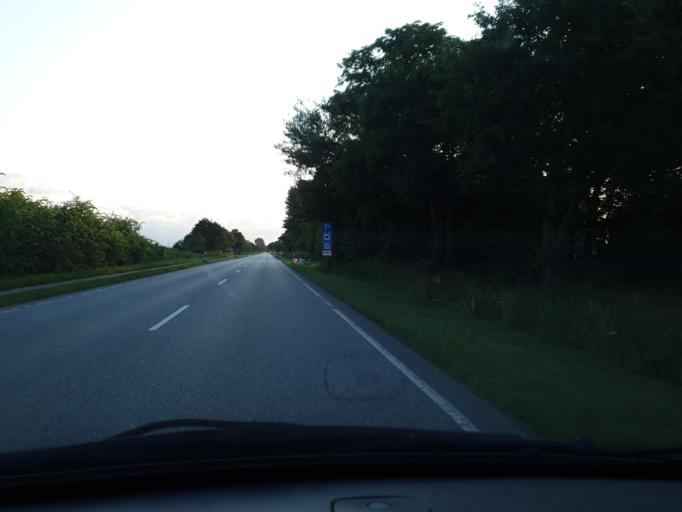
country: DE
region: Schleswig-Holstein
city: Brunsbuttel
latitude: 53.9070
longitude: 9.0802
